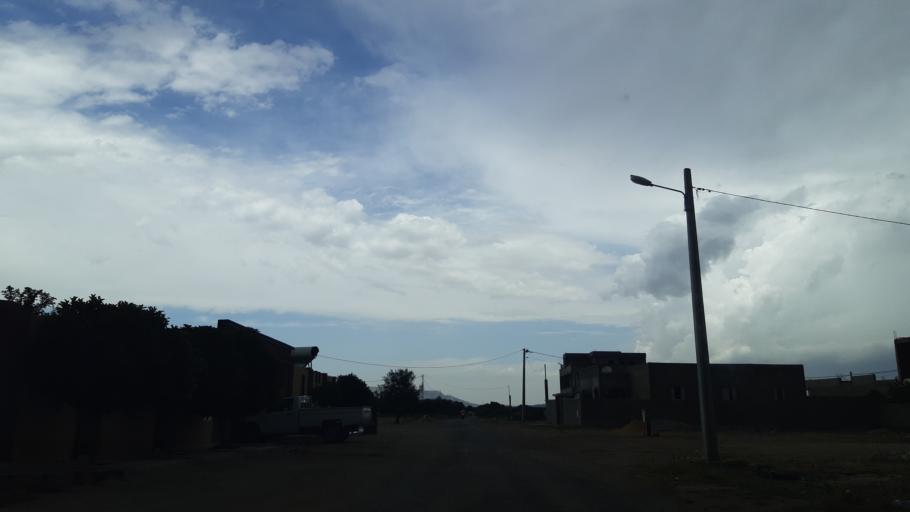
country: TN
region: Al Qayrawan
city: Sbikha
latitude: 36.1249
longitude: 10.0869
